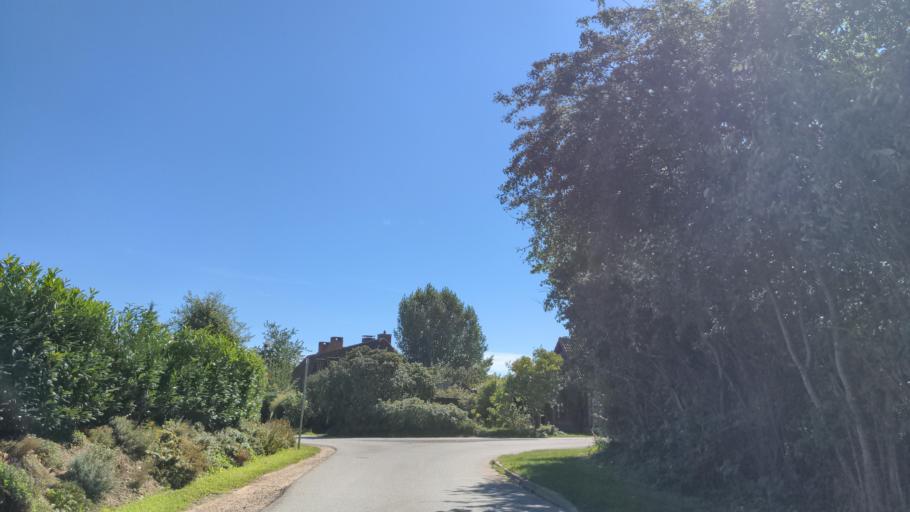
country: DE
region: Schleswig-Holstein
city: Altenkrempe
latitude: 54.1738
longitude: 10.8079
